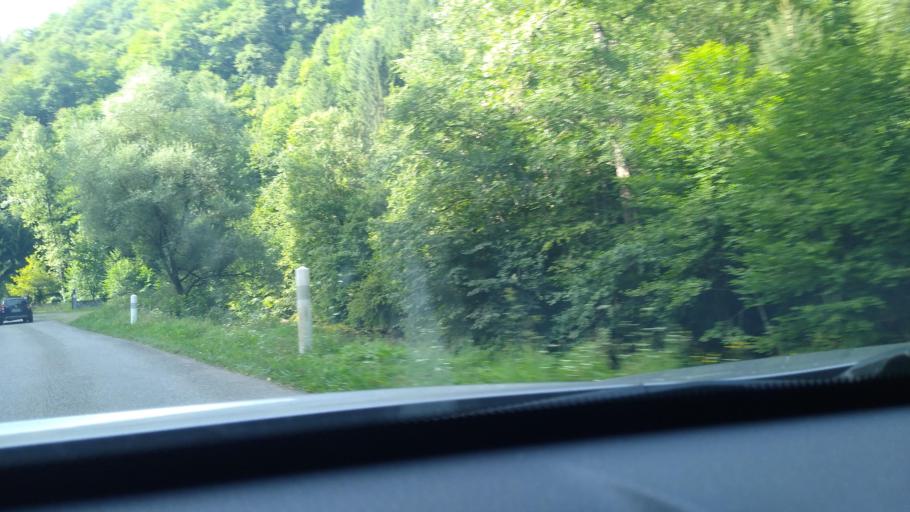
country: FR
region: Midi-Pyrenees
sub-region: Departement de l'Ariege
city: Saint-Girons
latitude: 42.8356
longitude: 1.1959
